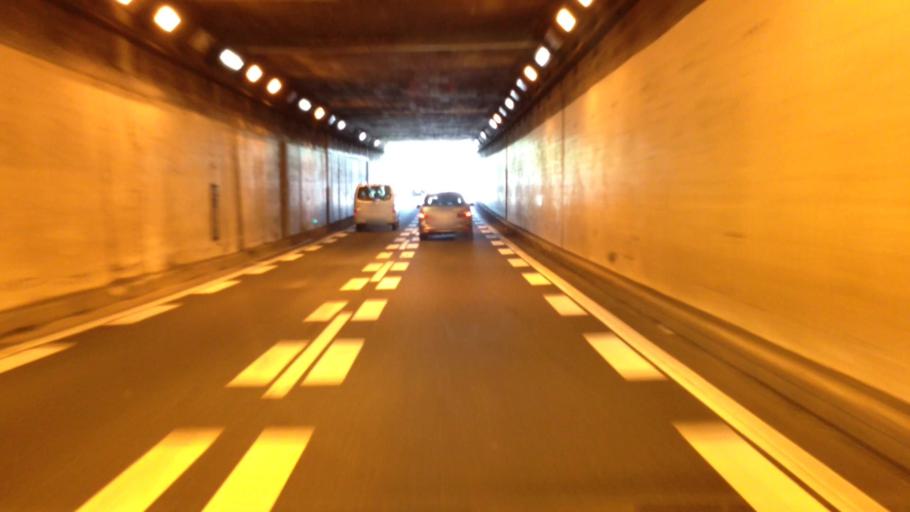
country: JP
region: Kanagawa
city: Yokohama
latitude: 35.4794
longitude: 139.5961
